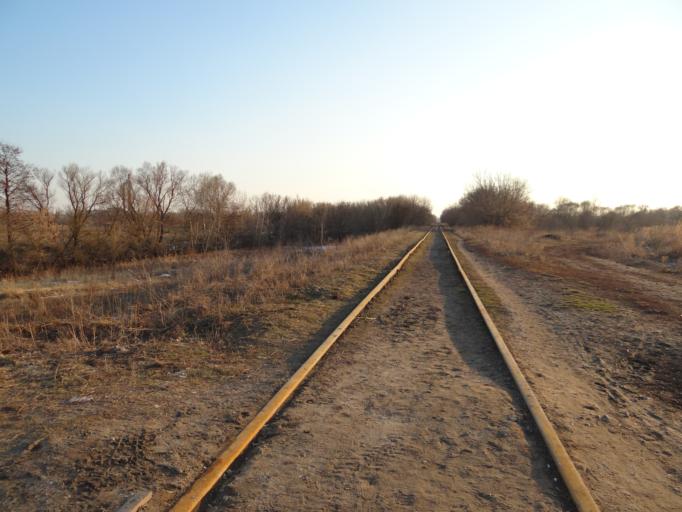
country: RU
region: Kursk
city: Kursk
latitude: 51.6843
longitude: 36.1112
